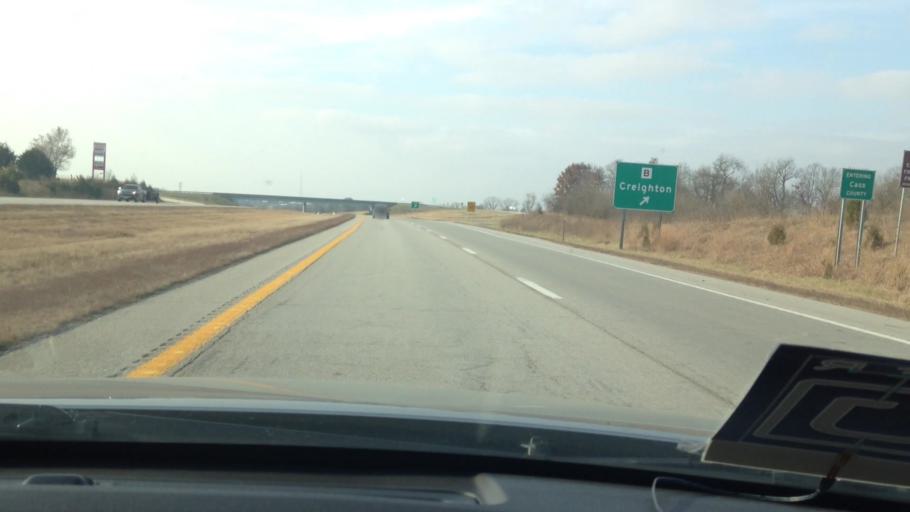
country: US
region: Missouri
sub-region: Cass County
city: Garden City
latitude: 38.4994
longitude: -94.0668
